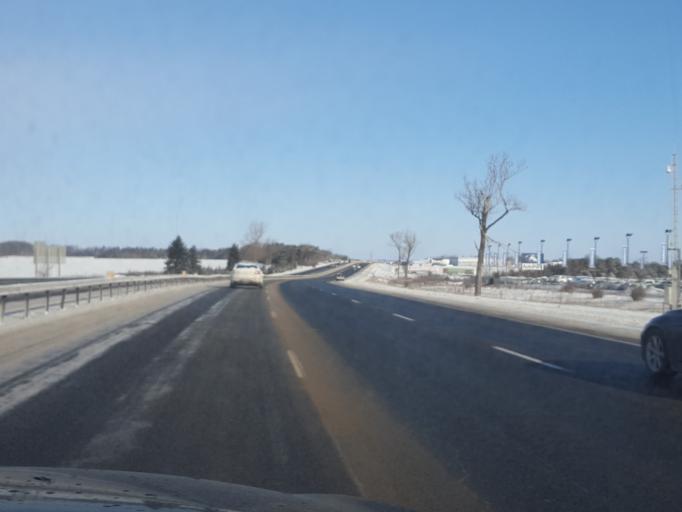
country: CA
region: Ontario
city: Innisfil
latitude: 44.3007
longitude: -79.6837
